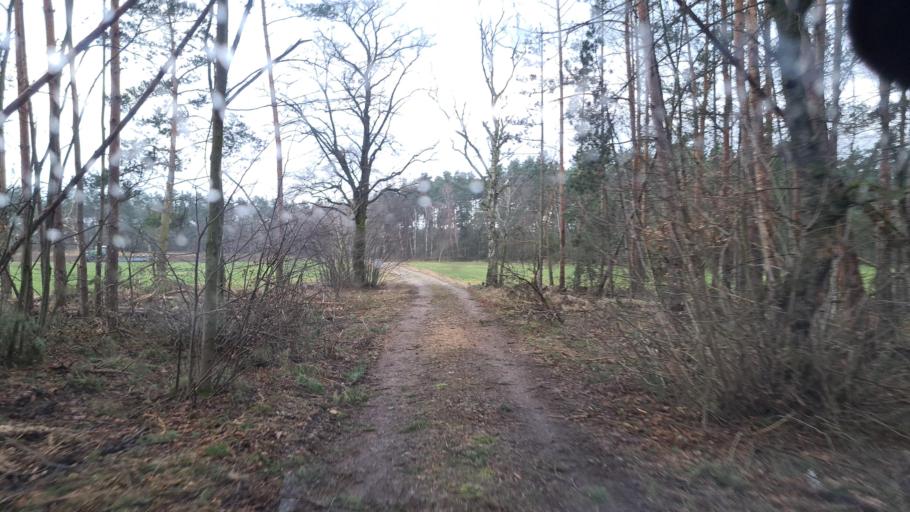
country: DE
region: Brandenburg
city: Kroppen
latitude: 51.3968
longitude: 13.7767
